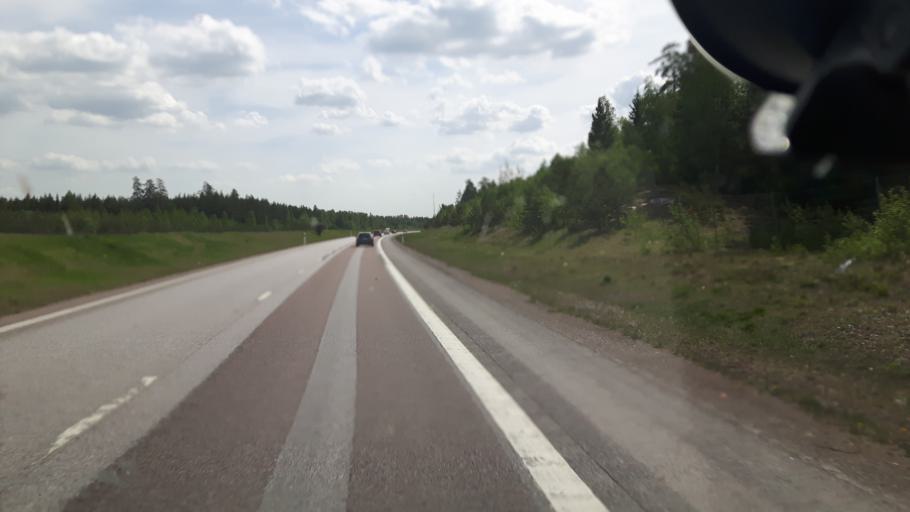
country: SE
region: Uppsala
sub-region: Osthammars Kommun
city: Bjorklinge
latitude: 60.0434
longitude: 17.6274
